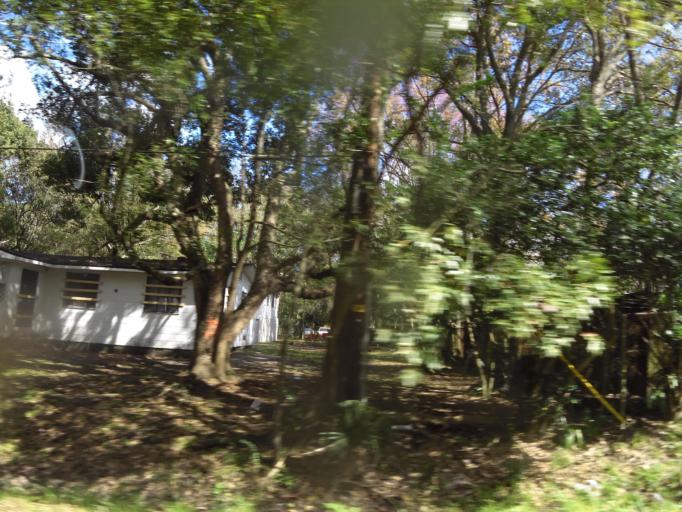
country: US
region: Florida
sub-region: Duval County
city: Jacksonville
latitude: 30.3305
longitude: -81.7182
